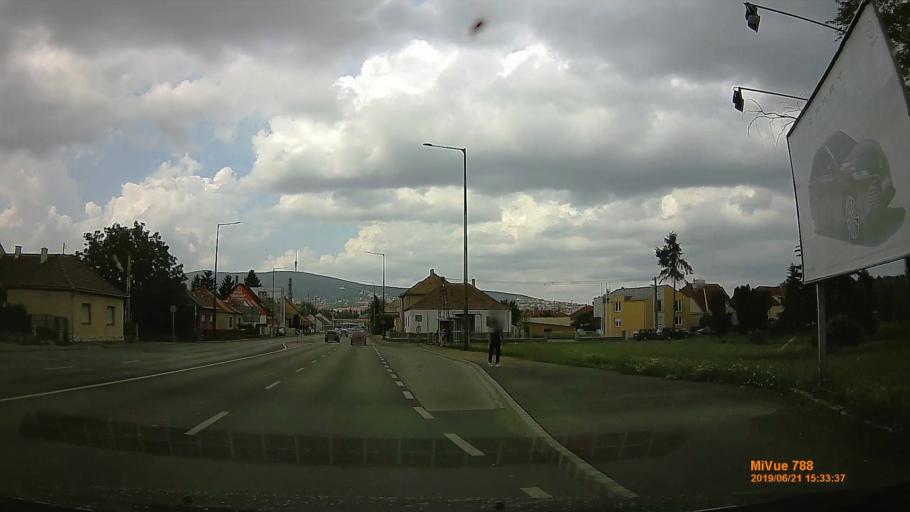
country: HU
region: Baranya
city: Pecs
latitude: 46.0570
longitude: 18.2309
